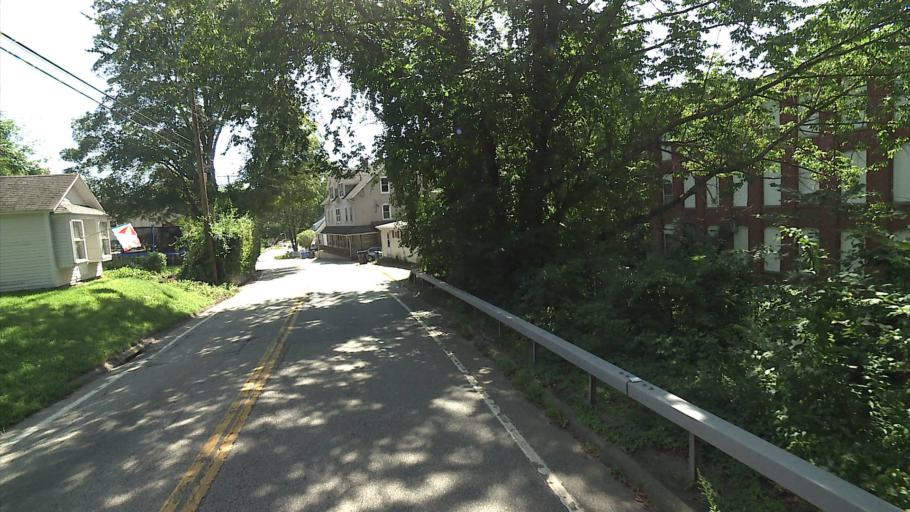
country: US
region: Connecticut
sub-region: New London County
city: Baltic
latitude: 41.6170
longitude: -72.0915
